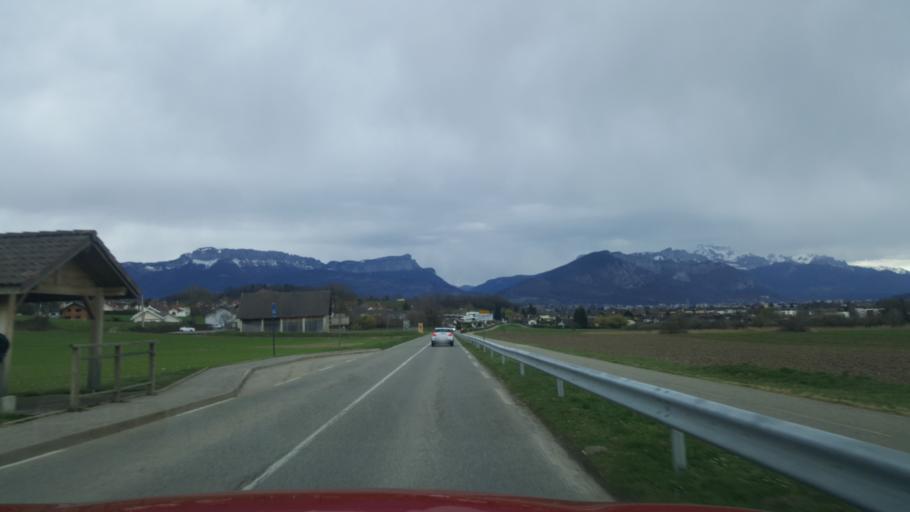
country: FR
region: Rhone-Alpes
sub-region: Departement de la Haute-Savoie
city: Epagny
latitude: 45.9448
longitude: 6.0774
